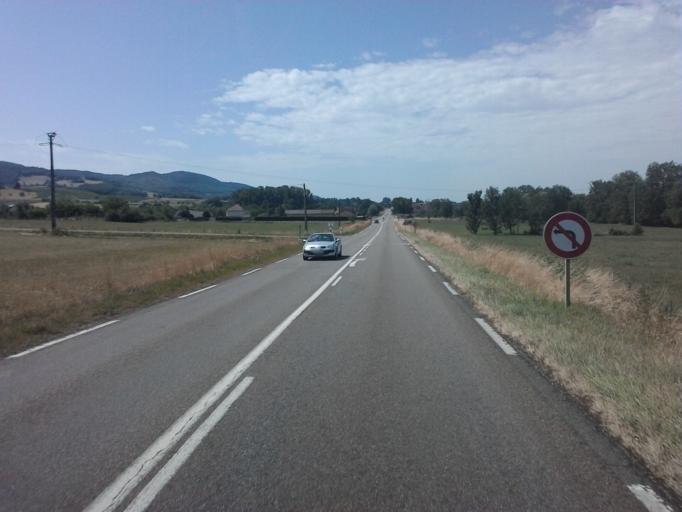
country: FR
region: Franche-Comte
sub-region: Departement du Jura
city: Montmorot
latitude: 46.6070
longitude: 5.4698
